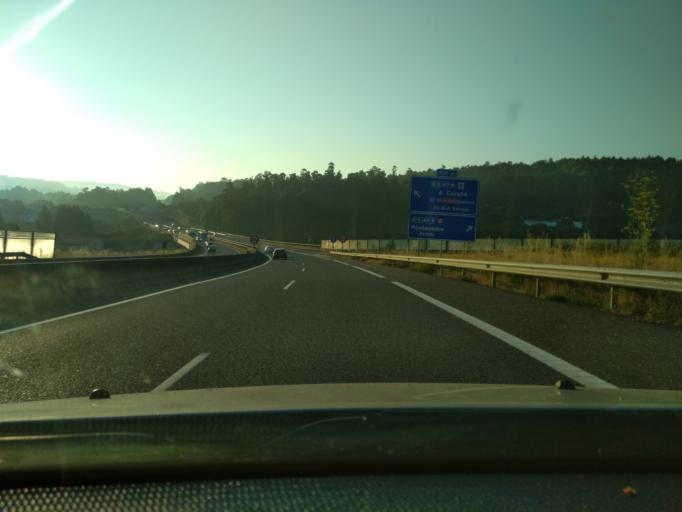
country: ES
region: Galicia
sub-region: Provincia da Coruna
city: Santiago de Compostela
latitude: 42.8561
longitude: -8.5749
